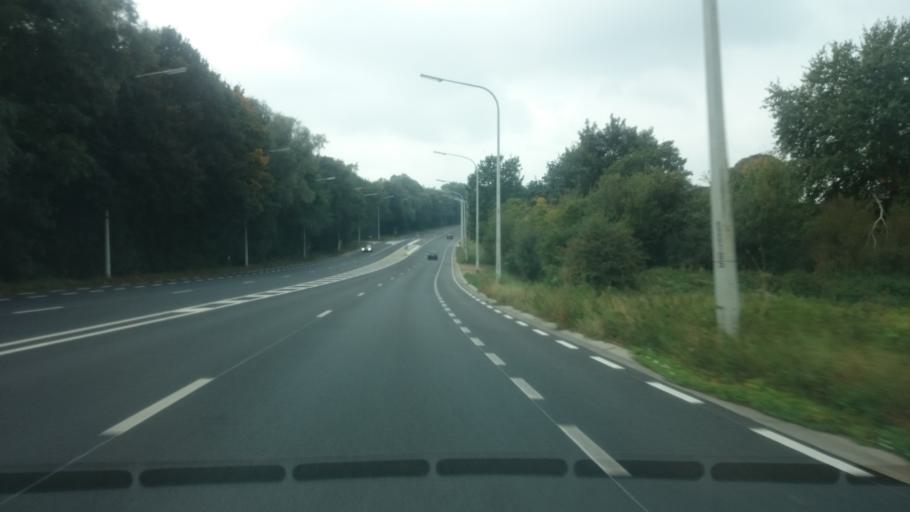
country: BE
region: Wallonia
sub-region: Province de Namur
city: Floreffe
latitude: 50.4767
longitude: 4.8036
